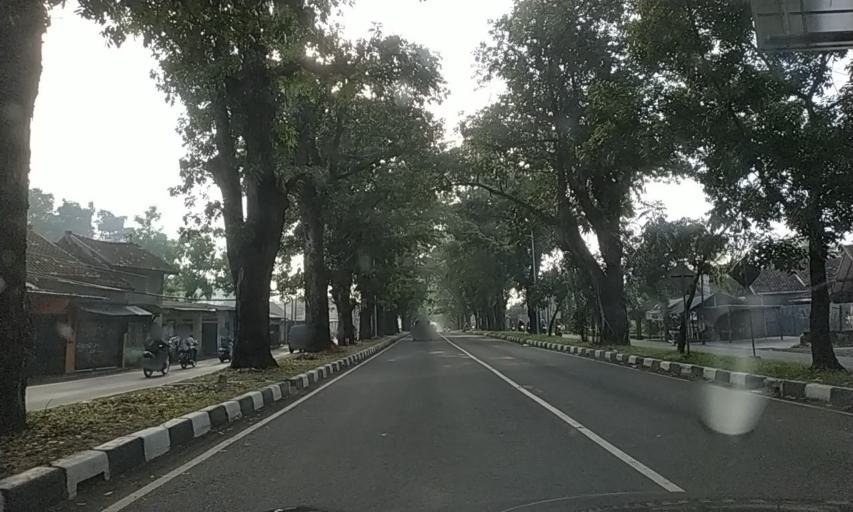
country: ID
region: Central Java
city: Candi Prambanan
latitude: -7.7569
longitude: 110.4814
